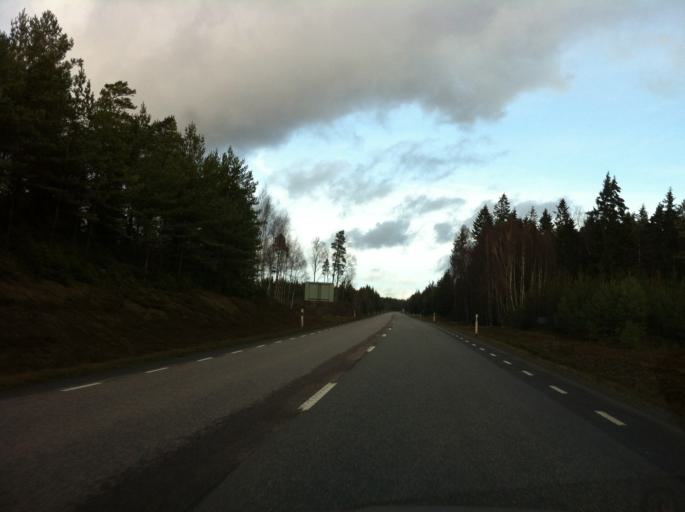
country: SE
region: Kronoberg
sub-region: Almhults Kommun
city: AElmhult
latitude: 56.5501
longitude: 14.1656
